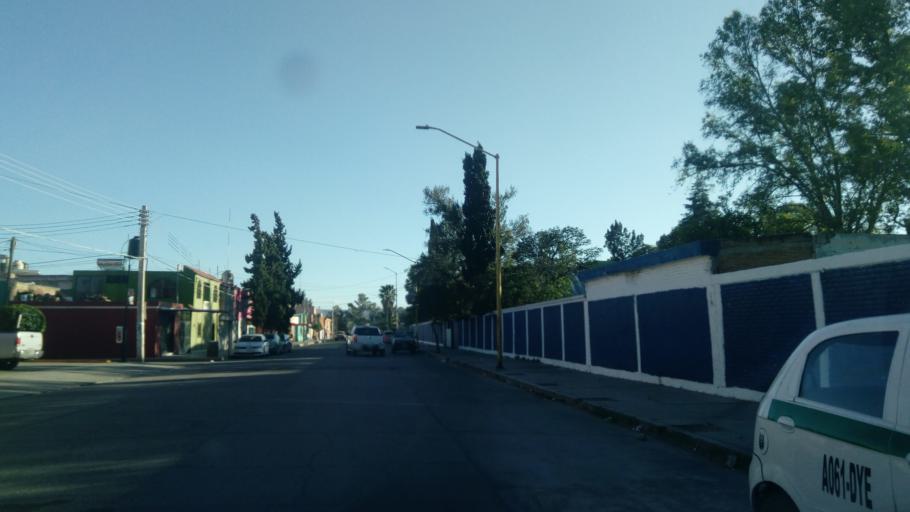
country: MX
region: Durango
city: Victoria de Durango
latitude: 24.0000
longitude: -104.6776
